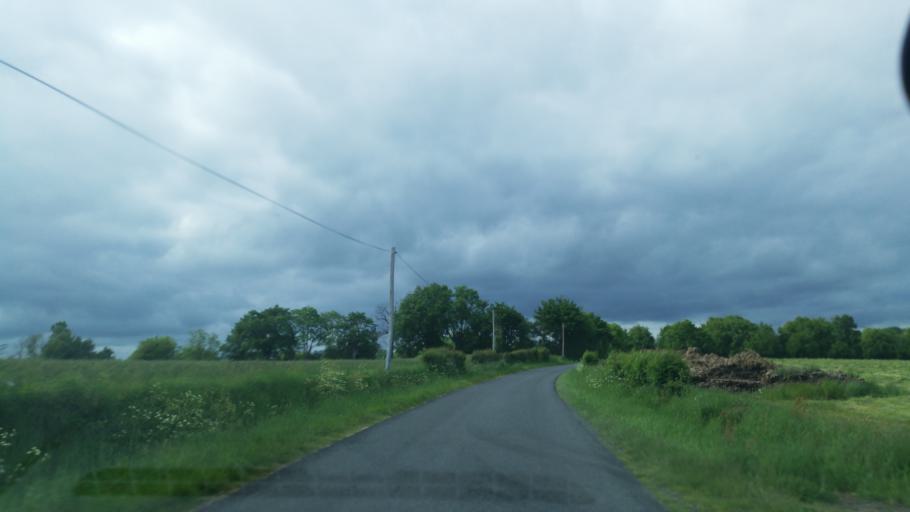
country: FR
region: Poitou-Charentes
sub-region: Departement des Deux-Sevres
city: Moncoutant
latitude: 46.7126
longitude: -0.5877
